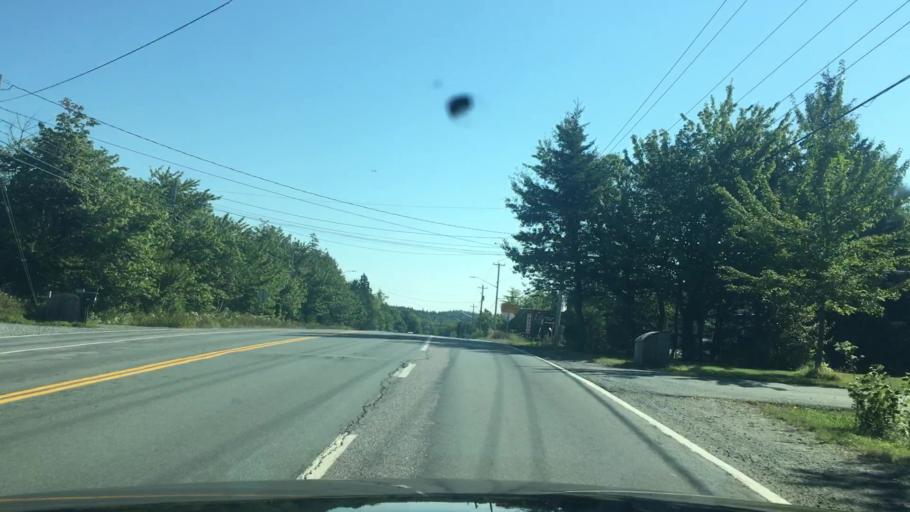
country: CA
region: Nova Scotia
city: Cole Harbour
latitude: 44.7781
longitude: -63.0889
